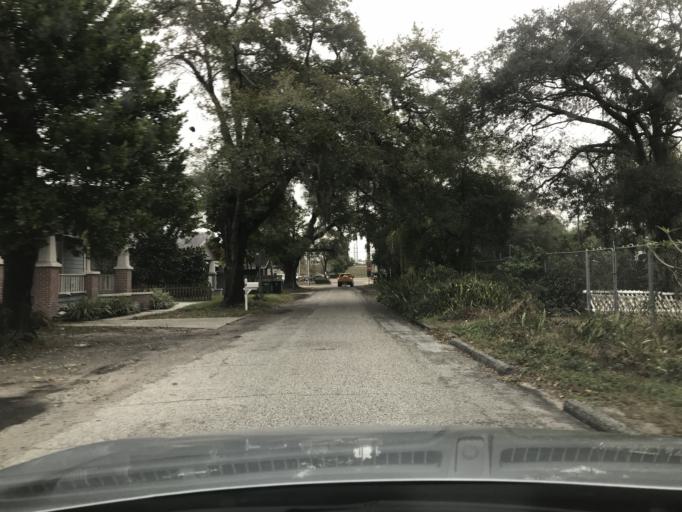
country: US
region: Florida
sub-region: Hillsborough County
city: Tampa
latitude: 27.9808
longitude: -82.4562
